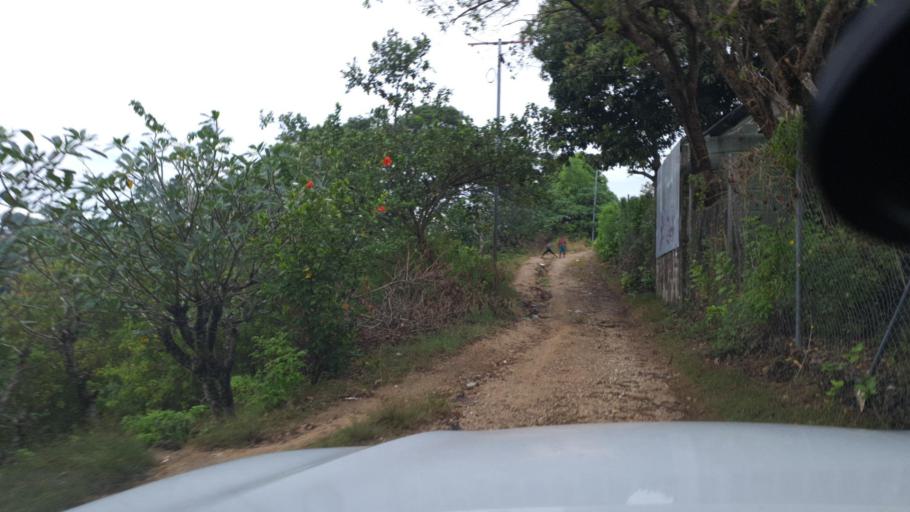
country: SB
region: Guadalcanal
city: Honiara
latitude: -9.4419
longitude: 159.9693
